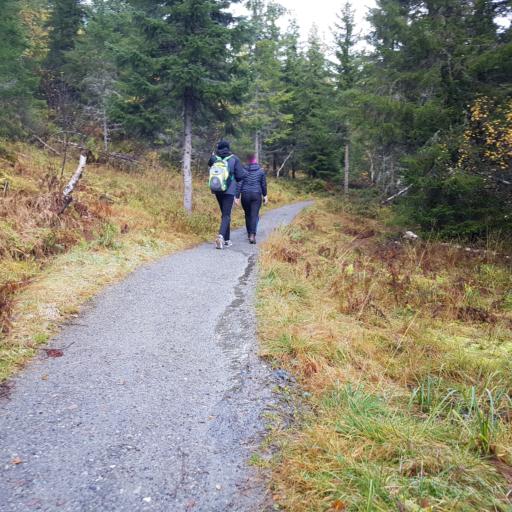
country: NO
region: Sor-Trondelag
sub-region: Trondheim
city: Trondheim
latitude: 63.4235
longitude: 10.2773
